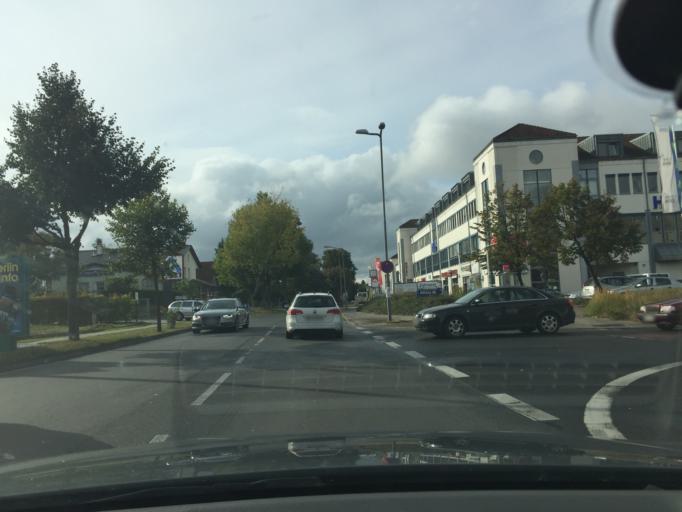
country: DE
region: Berlin
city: Hellersdorf
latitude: 52.5377
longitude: 13.6345
